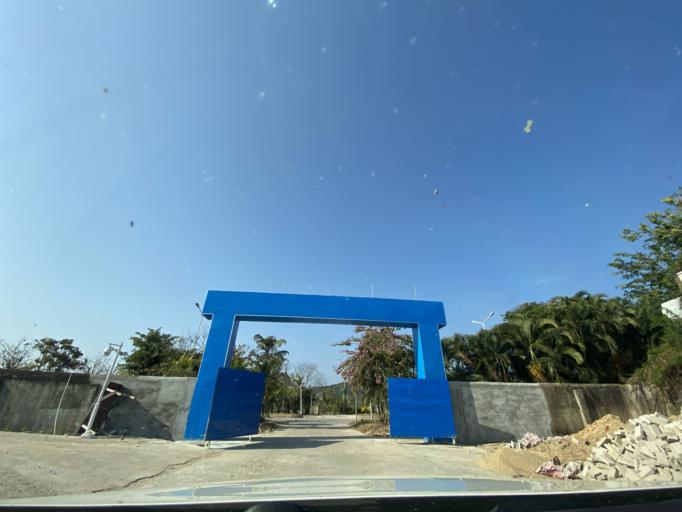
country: CN
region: Hainan
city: Haitangwan
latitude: 18.4027
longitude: 109.7655
